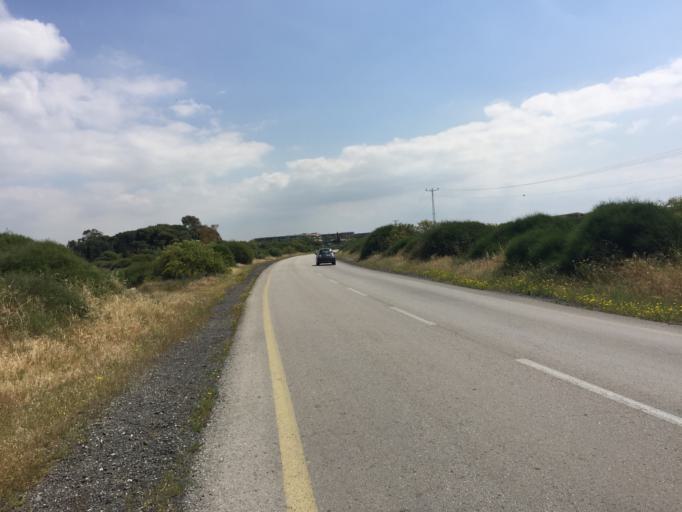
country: IL
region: Haifa
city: Qesarya
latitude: 32.4942
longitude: 34.8975
